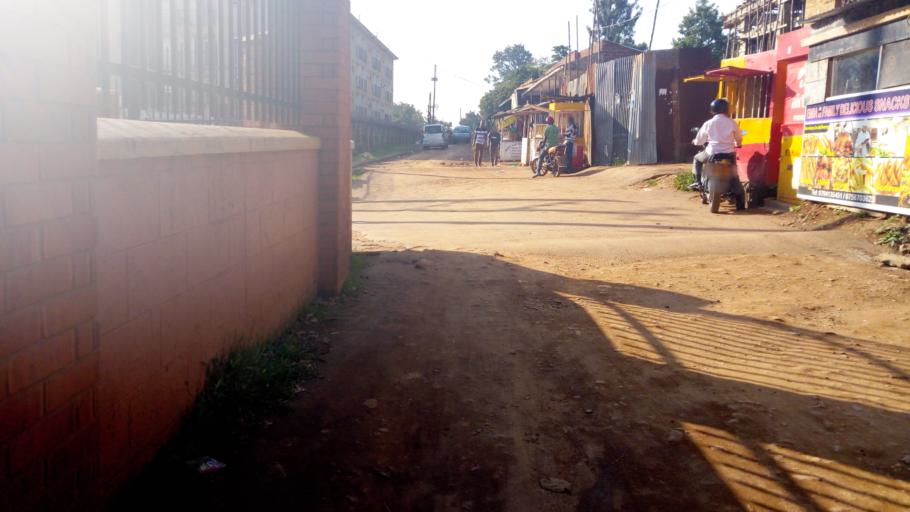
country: UG
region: Central Region
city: Kampala Central Division
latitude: 0.3354
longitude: 32.5611
